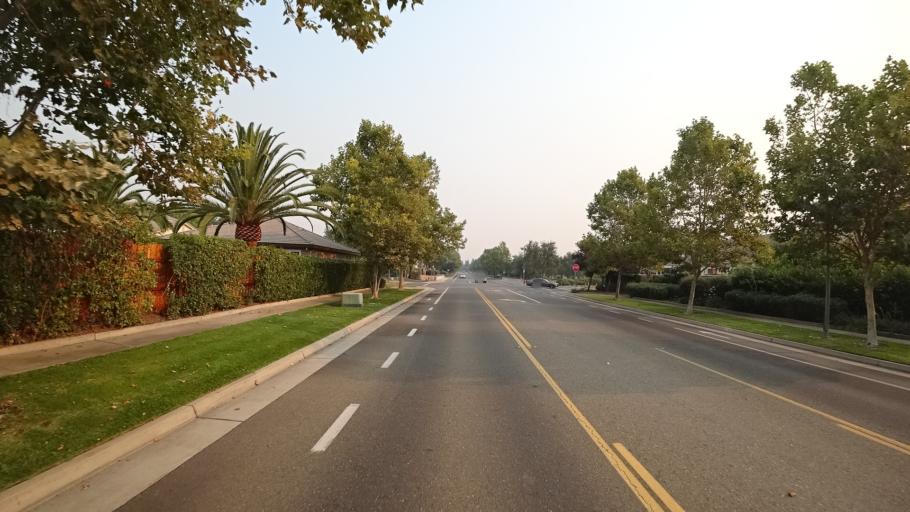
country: US
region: California
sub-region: Sacramento County
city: Laguna
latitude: 38.4044
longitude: -121.4408
